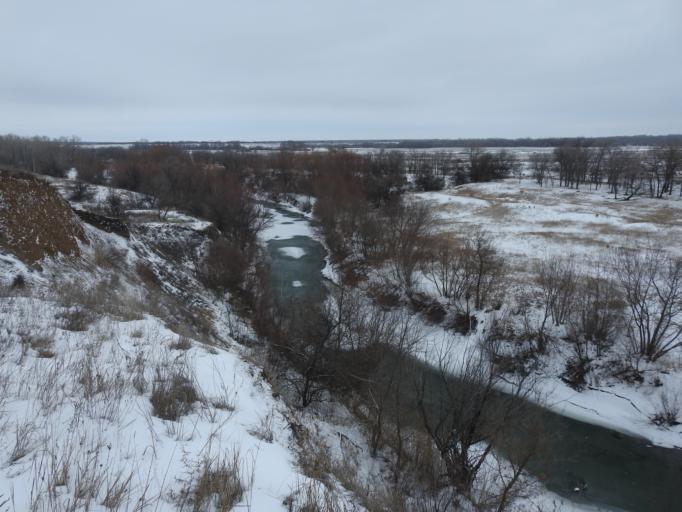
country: RU
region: Saratov
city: Krasnyy Yar
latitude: 51.5523
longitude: 46.5145
